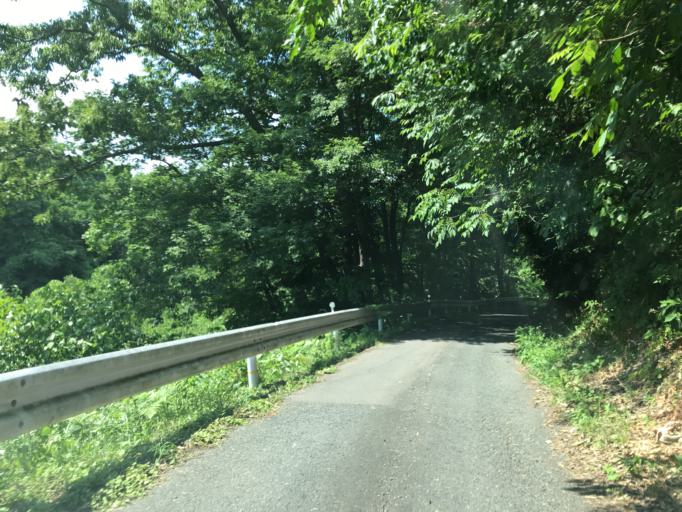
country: JP
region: Fukushima
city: Yanagawamachi-saiwaicho
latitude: 37.7796
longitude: 140.6551
